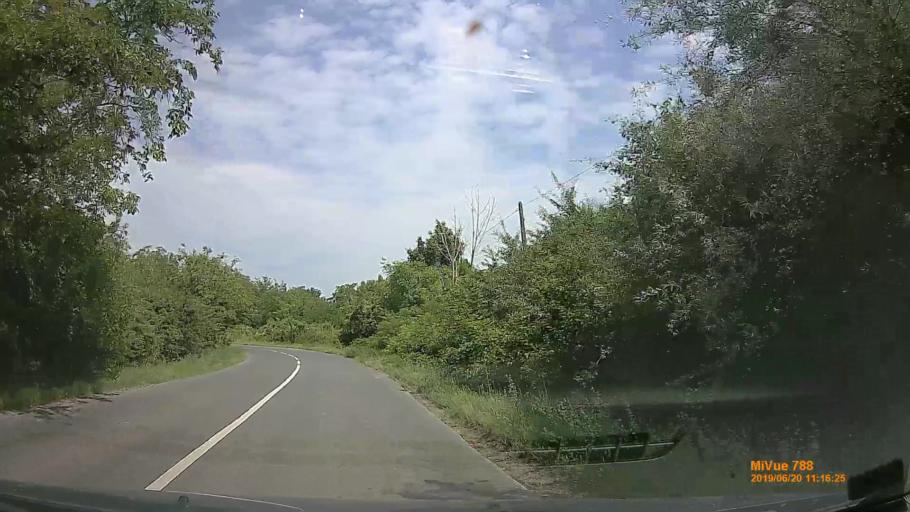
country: HU
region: Baranya
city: Pecsvarad
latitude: 46.1533
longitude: 18.4791
